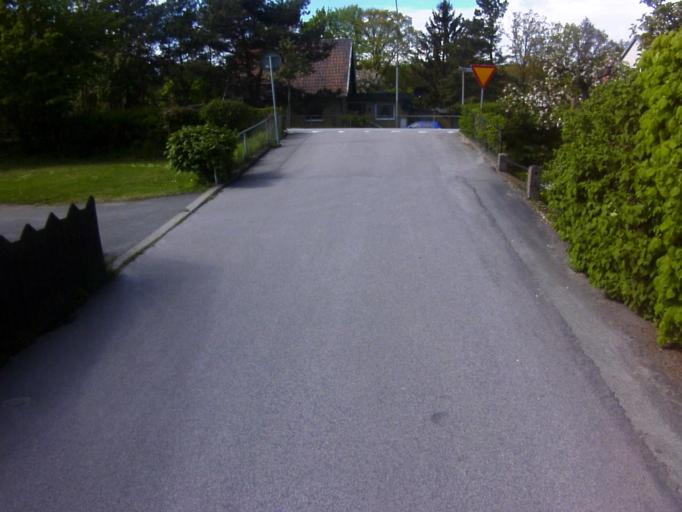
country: SE
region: Blekinge
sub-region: Solvesborgs Kommun
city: Soelvesborg
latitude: 56.0596
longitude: 14.5999
